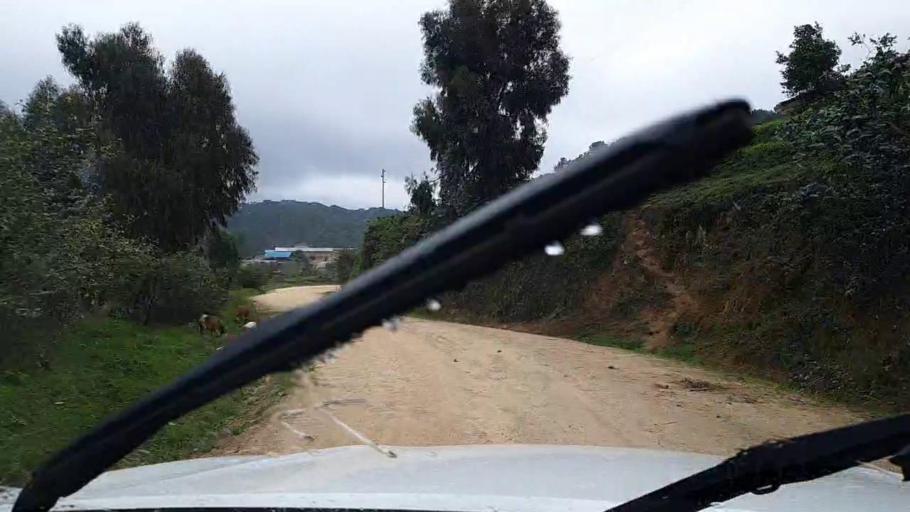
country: RW
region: Southern Province
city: Nzega
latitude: -2.3706
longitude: 29.3830
